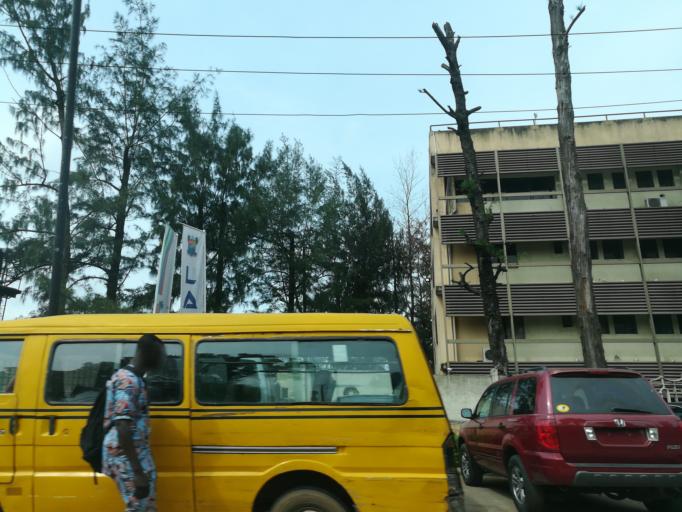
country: NG
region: Lagos
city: Ojota
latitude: 6.6008
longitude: 3.3744
